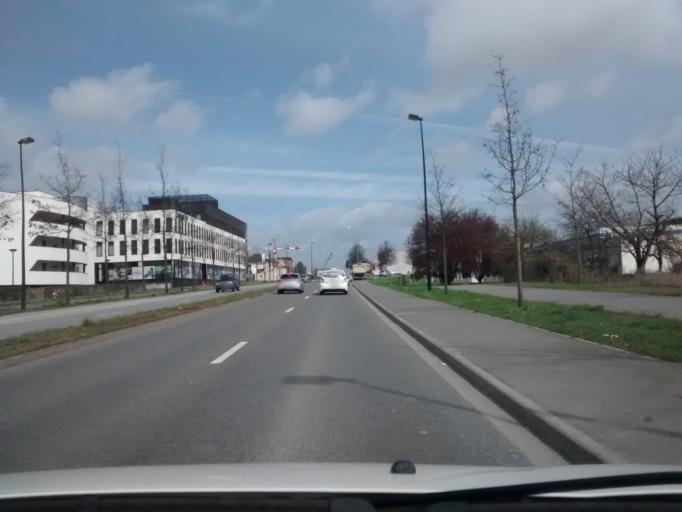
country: FR
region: Brittany
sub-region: Departement d'Ille-et-Vilaine
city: Saint-Jacques-de-la-Lande
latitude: 48.0852
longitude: -1.7085
